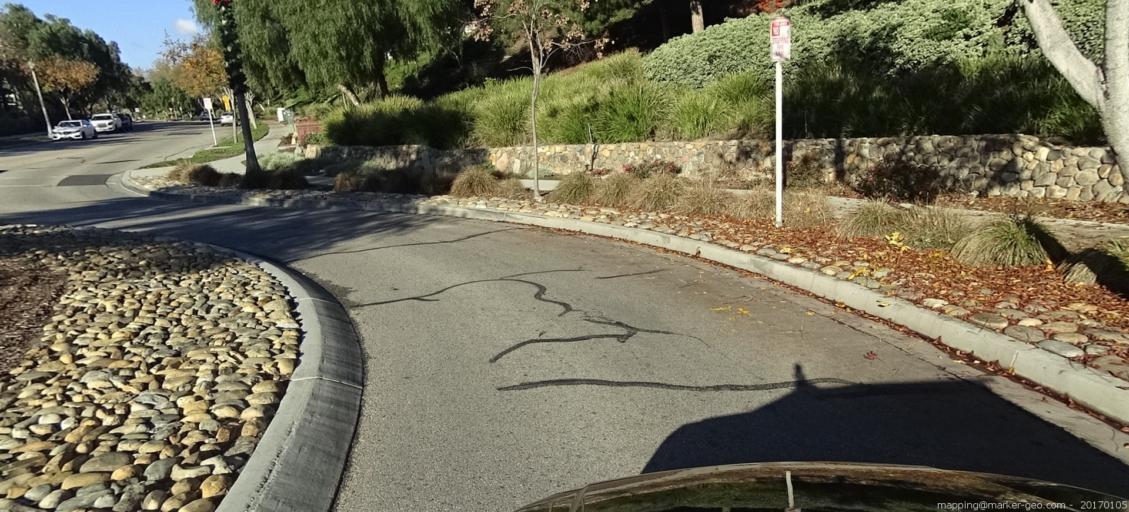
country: US
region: California
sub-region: Orange County
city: Ladera Ranch
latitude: 33.5376
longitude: -117.6435
